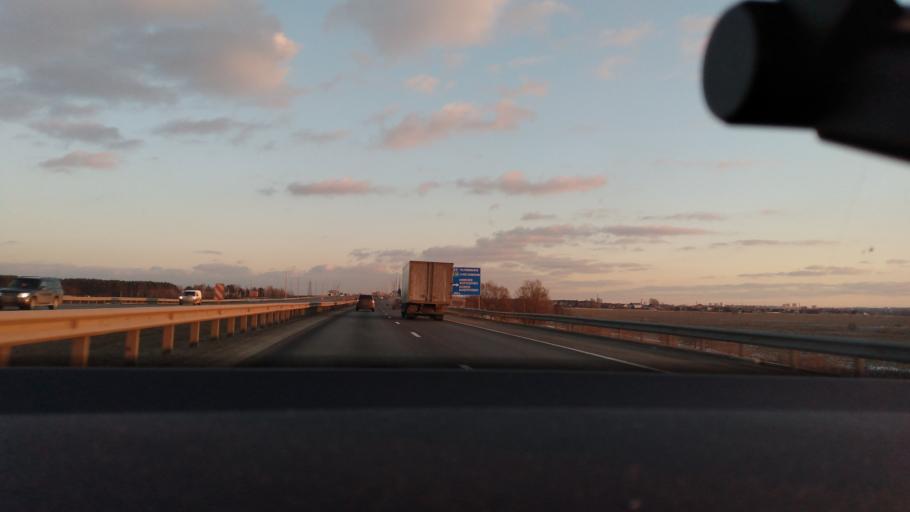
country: RU
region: Moskovskaya
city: Raduzhnyy
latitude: 55.1363
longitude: 38.7679
